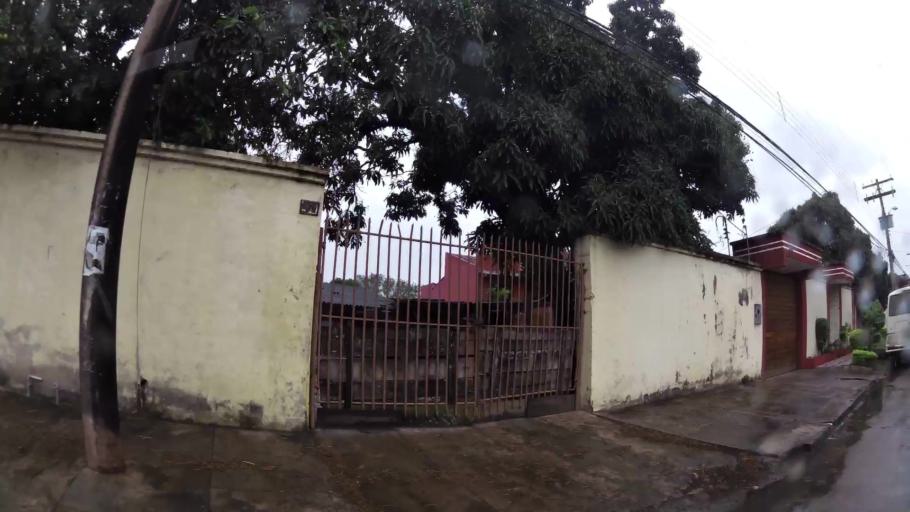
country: BO
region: Santa Cruz
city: Santa Cruz de la Sierra
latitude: -17.7959
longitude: -63.1585
